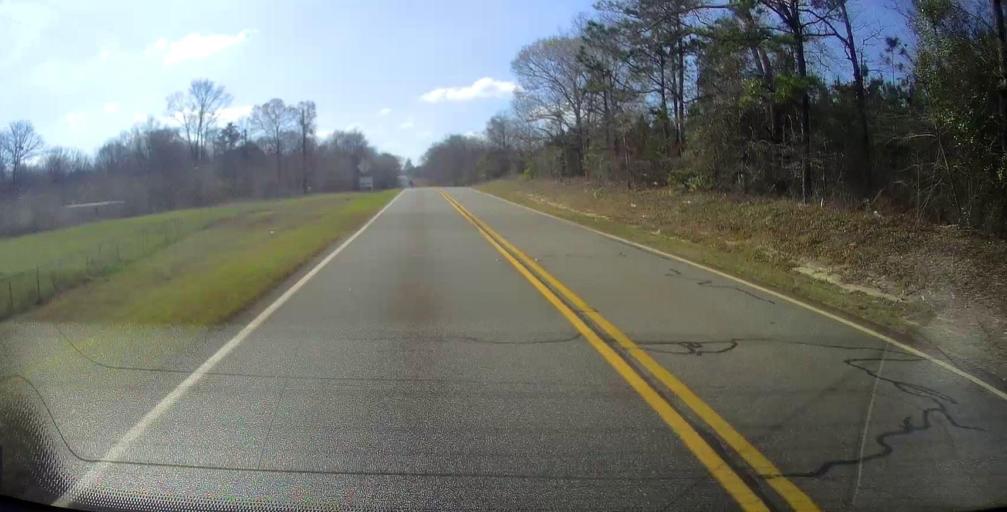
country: US
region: Georgia
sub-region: Twiggs County
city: Jeffersonville
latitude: 32.6812
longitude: -83.2827
